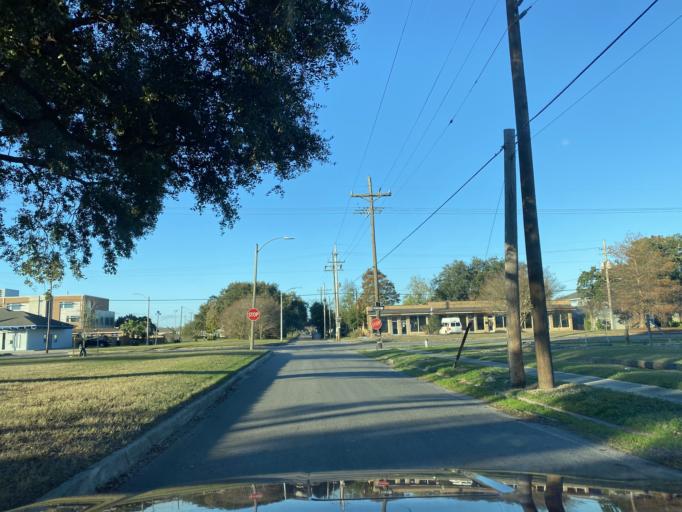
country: US
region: Louisiana
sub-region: Orleans Parish
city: New Orleans
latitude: 30.0165
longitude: -90.0558
